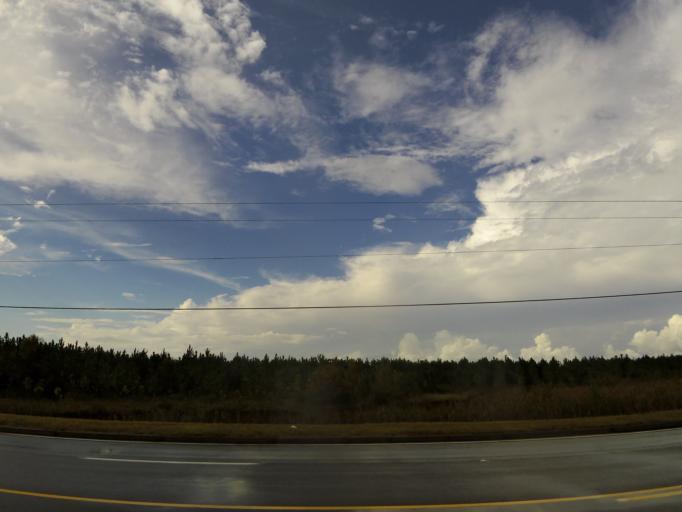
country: US
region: Georgia
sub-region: Long County
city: Ludowici
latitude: 31.7225
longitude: -81.7286
